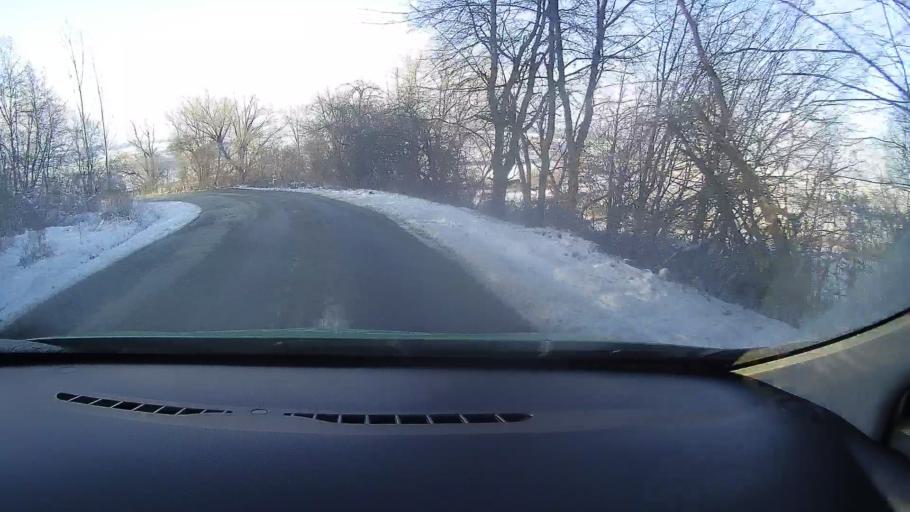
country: RO
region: Sibiu
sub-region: Oras Agnita
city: Ruja
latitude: 45.9884
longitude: 24.6713
